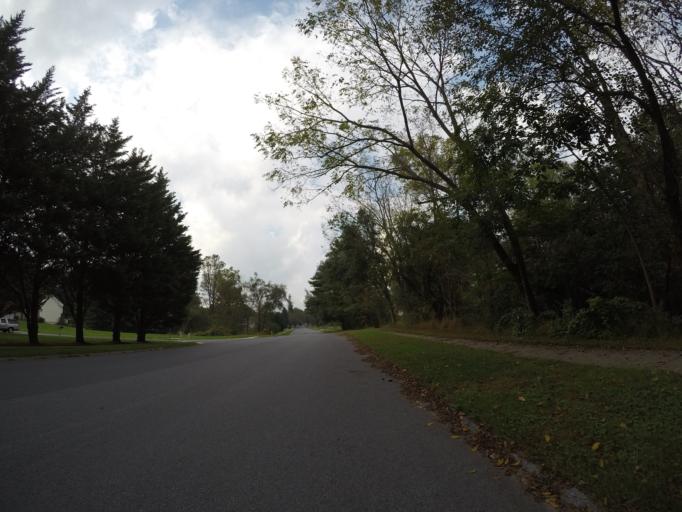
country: US
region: Maryland
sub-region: Howard County
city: Columbia
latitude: 39.2617
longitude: -76.8558
